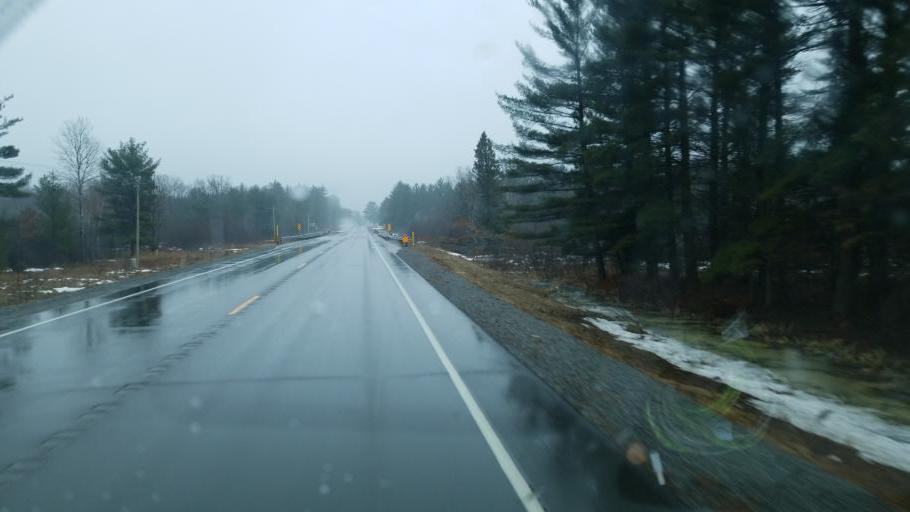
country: US
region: Wisconsin
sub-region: Clark County
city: Neillsville
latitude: 44.4829
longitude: -90.3557
